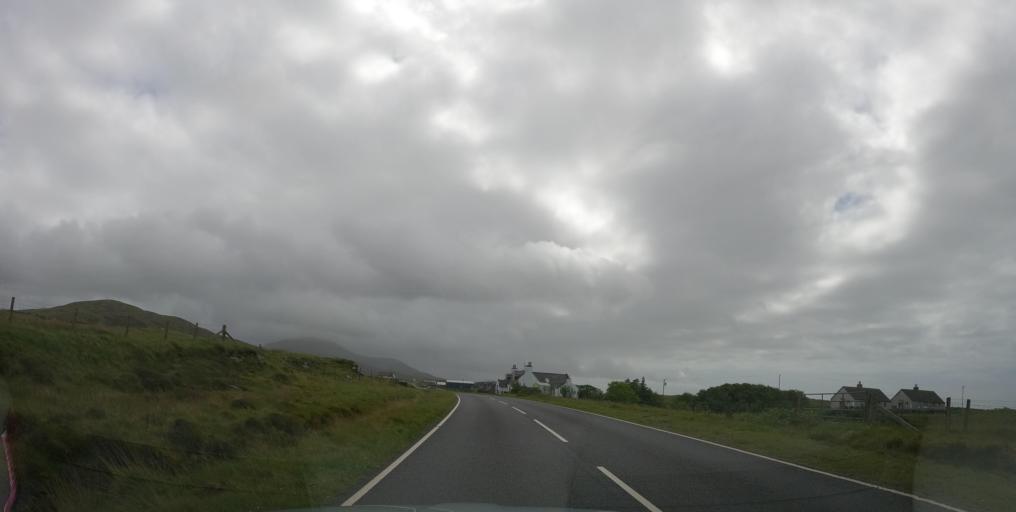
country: GB
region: Scotland
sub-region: Eilean Siar
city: Isle of South Uist
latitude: 57.3023
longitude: -7.3721
